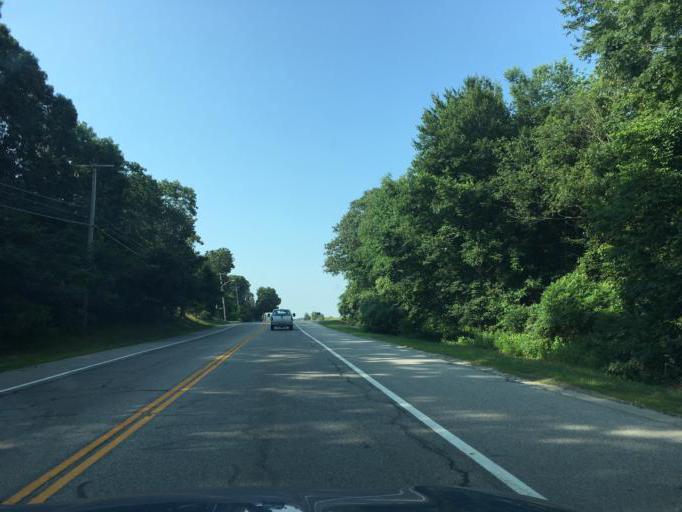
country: US
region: Rhode Island
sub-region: Washington County
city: Exeter
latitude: 41.5713
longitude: -71.5169
